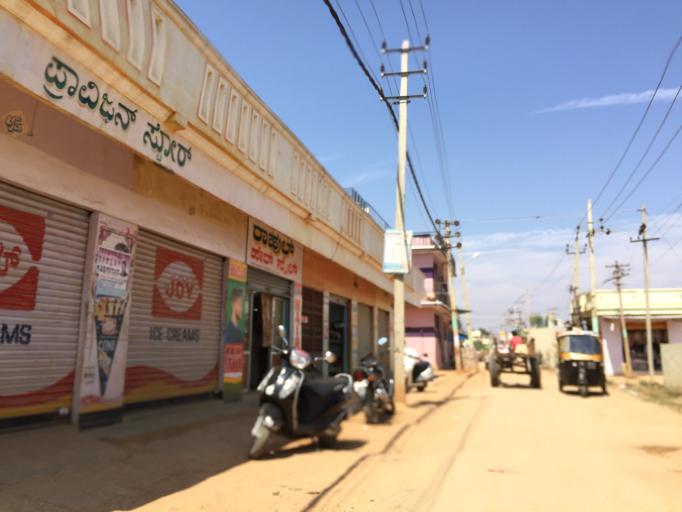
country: IN
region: Karnataka
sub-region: Kolar
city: Kolar
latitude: 13.1332
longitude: 78.1181
